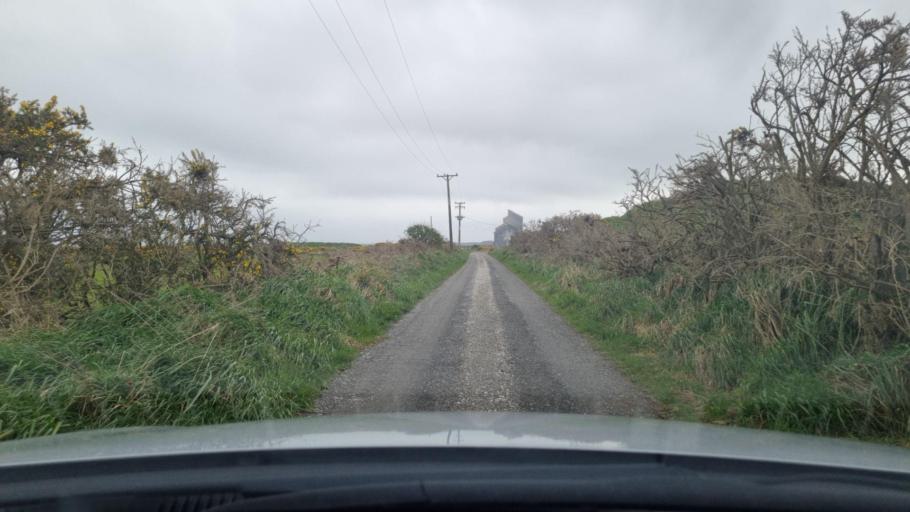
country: NZ
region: Southland
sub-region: Invercargill City
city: Invercargill
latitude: -46.4562
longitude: 168.3618
